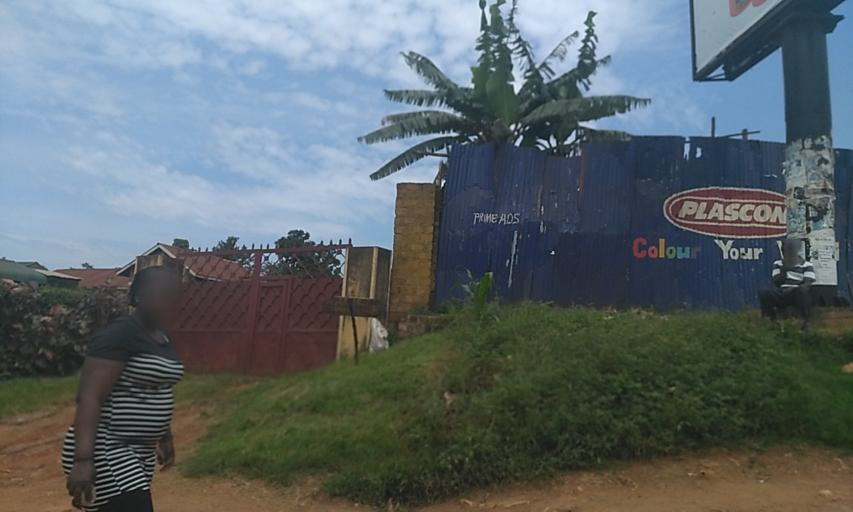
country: UG
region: Central Region
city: Kampala Central Division
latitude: 0.3005
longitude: 32.5355
